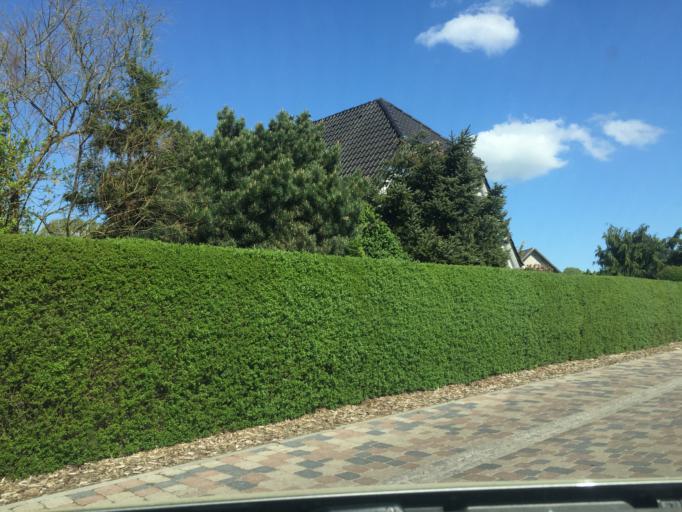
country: DE
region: Mecklenburg-Vorpommern
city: Torgelow
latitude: 53.6260
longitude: 14.0064
